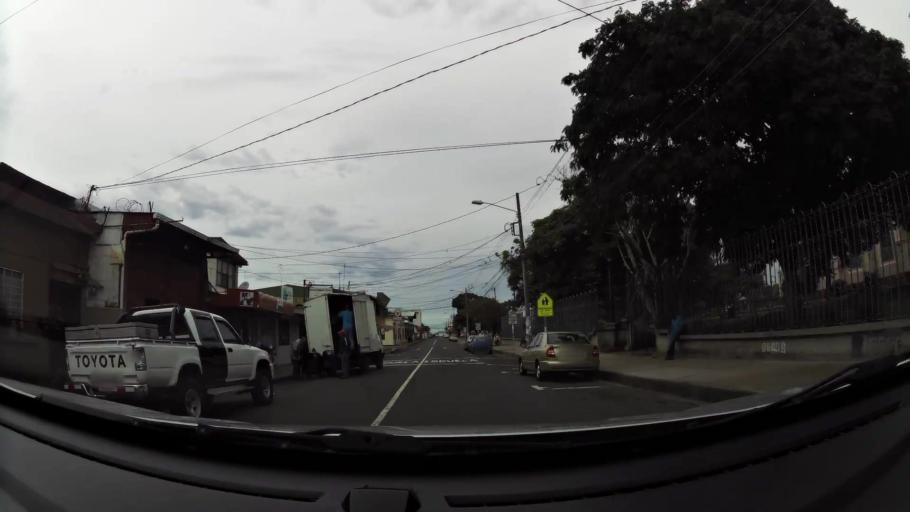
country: CR
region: San Jose
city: San Vicente de Moravia
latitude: 9.9612
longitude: -84.0483
